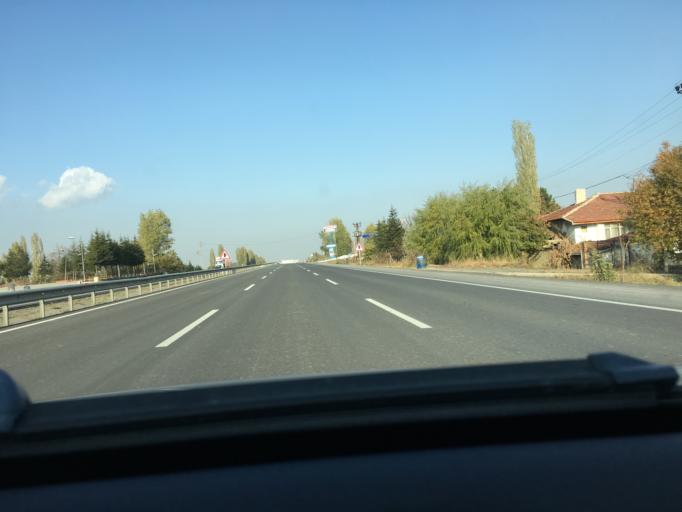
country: TR
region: Ankara
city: Polatli
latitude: 39.6703
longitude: 32.2306
